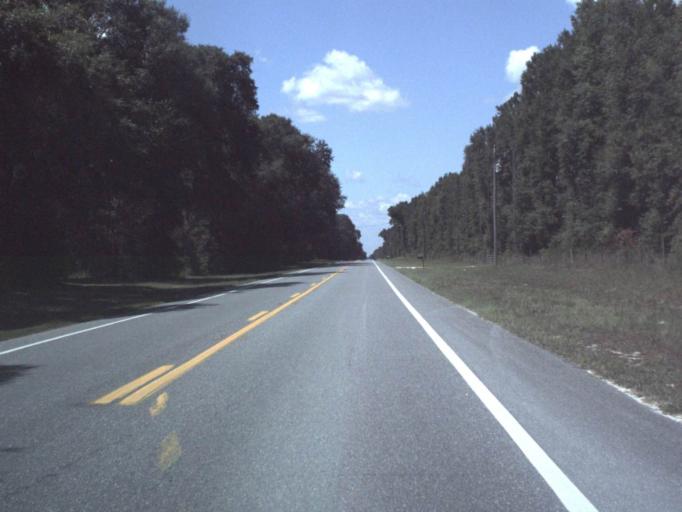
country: US
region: Florida
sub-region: Alachua County
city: High Springs
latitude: 29.7828
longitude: -82.7408
